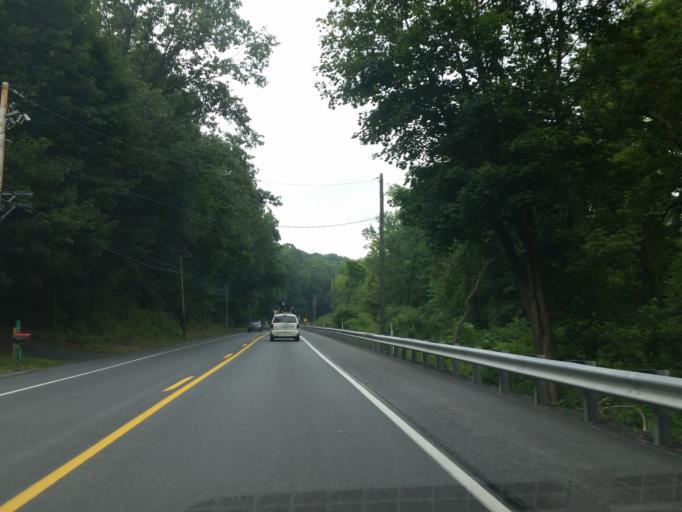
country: US
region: Pennsylvania
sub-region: Lancaster County
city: Brickerville
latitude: 40.2191
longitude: -76.3024
